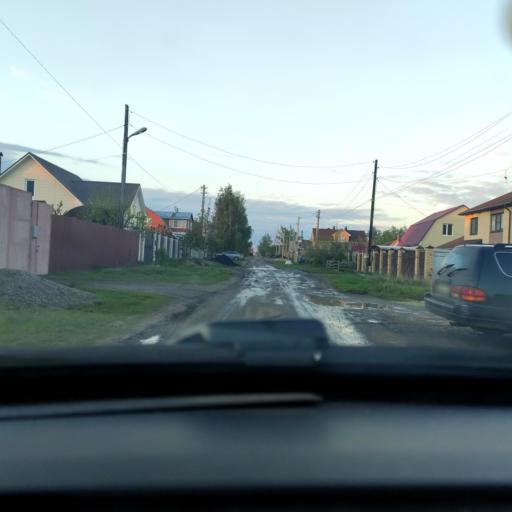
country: RU
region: Voronezj
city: Novaya Usman'
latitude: 51.6540
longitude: 39.4157
